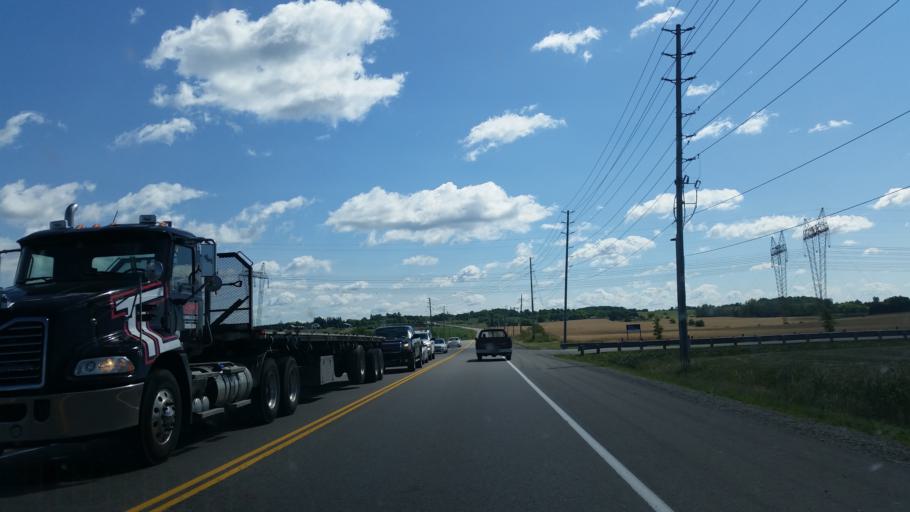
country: CA
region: Ontario
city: Vaughan
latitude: 43.8922
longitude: -79.6922
